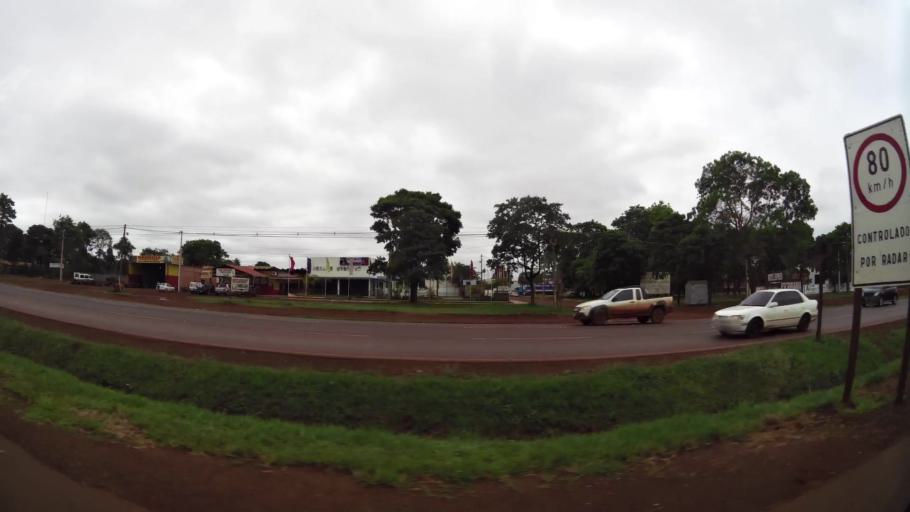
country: PY
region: Alto Parana
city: Ciudad del Este
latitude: -25.4926
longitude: -54.7307
